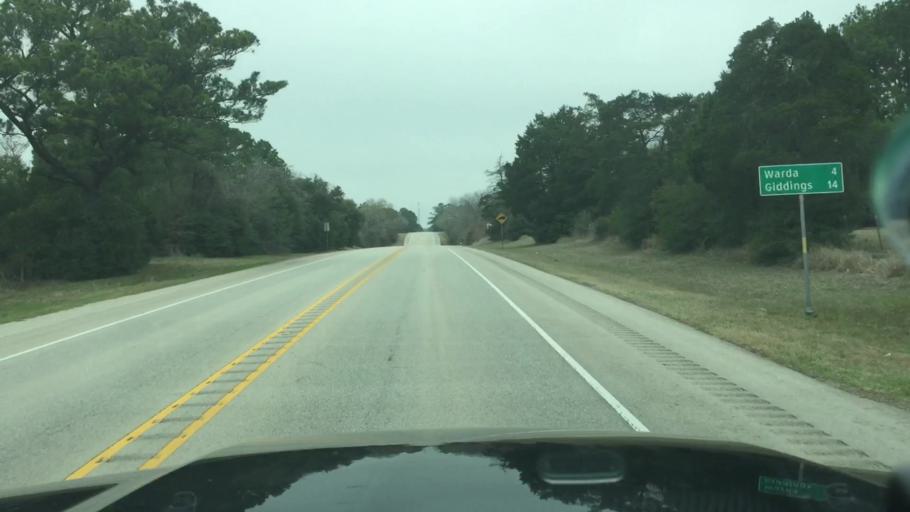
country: US
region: Texas
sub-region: Fayette County
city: La Grange
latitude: 30.0019
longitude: -96.8924
